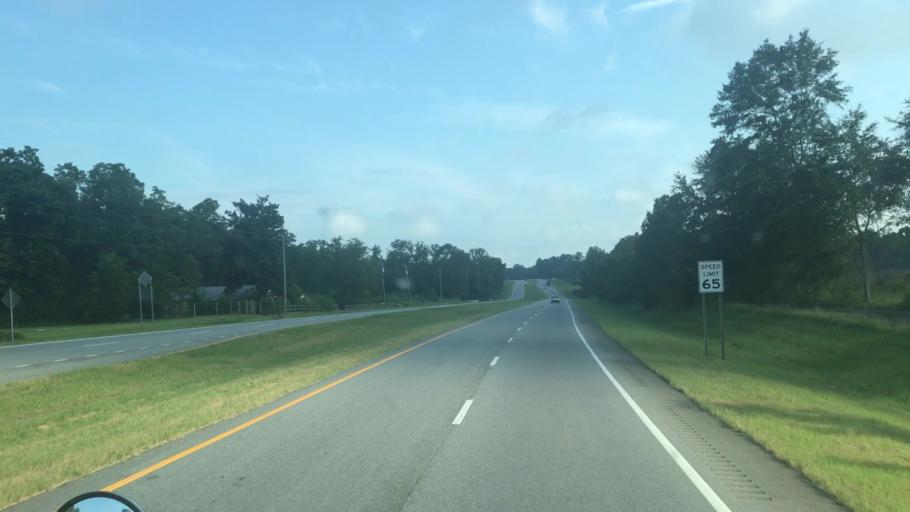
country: US
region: Georgia
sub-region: Decatur County
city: Bainbridge
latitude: 30.7782
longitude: -84.4893
